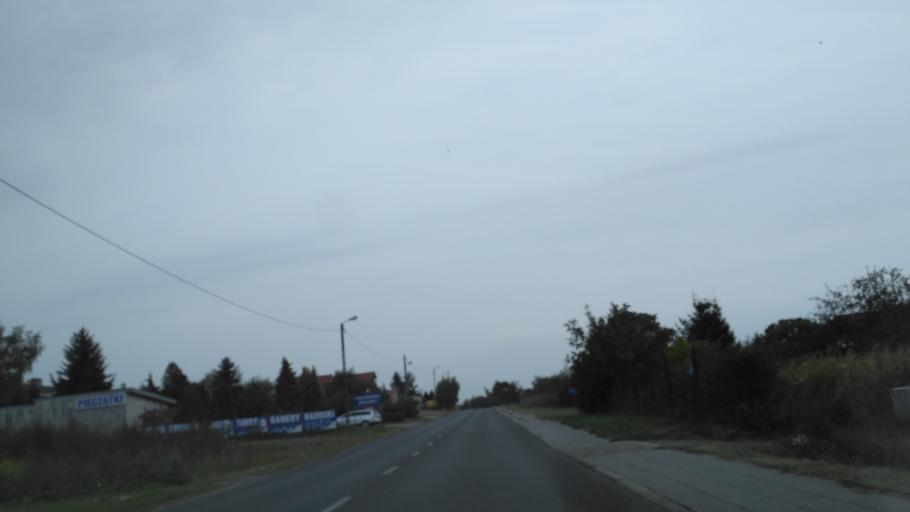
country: PL
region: Lublin Voivodeship
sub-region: Powiat lubelski
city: Lublin
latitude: 51.2175
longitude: 22.5900
